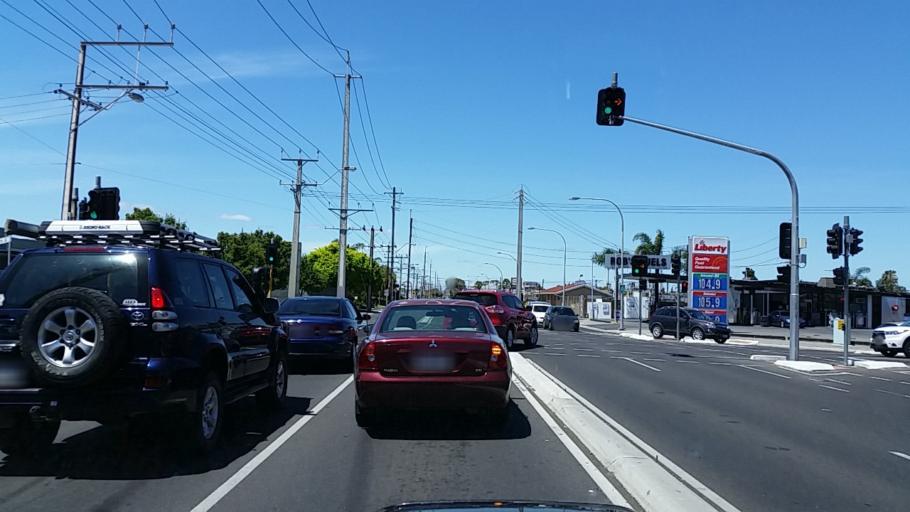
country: AU
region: South Australia
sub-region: Charles Sturt
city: Woodville West
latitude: -34.8907
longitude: 138.5315
